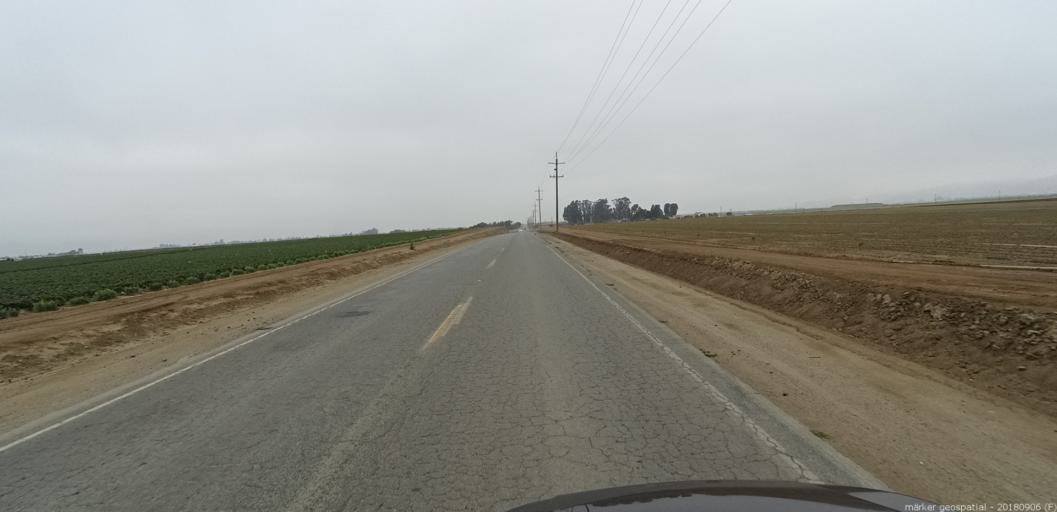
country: US
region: California
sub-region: Monterey County
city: Salinas
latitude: 36.6569
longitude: -121.5870
